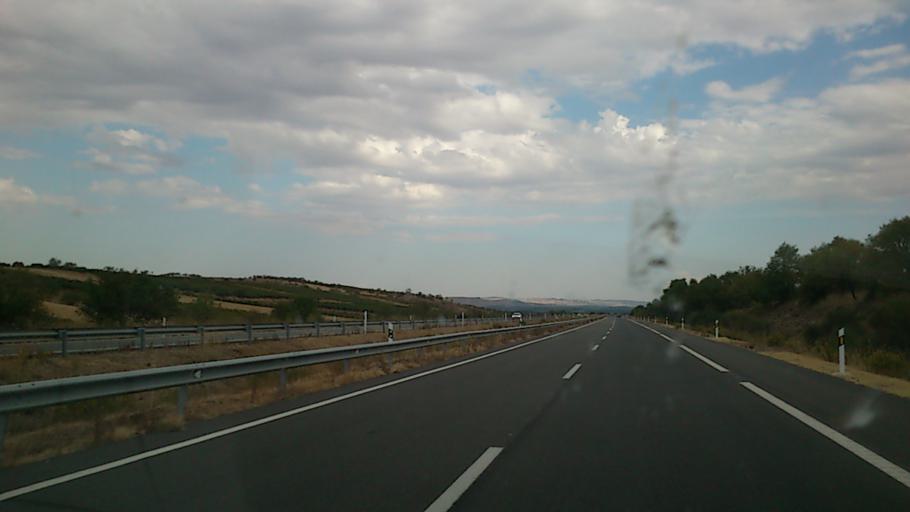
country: ES
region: La Rioja
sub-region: Provincia de La Rioja
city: Alcanadre
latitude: 42.3800
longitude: -2.1071
